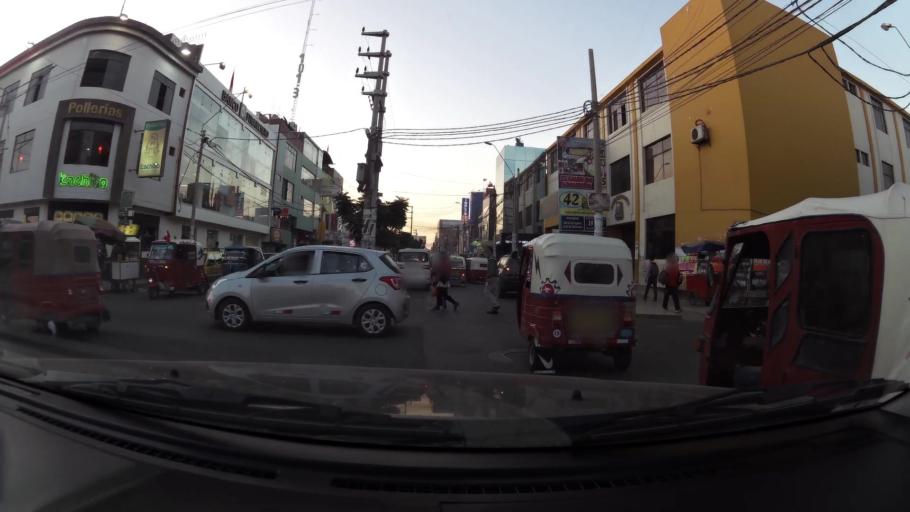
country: PE
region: Ica
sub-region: Provincia de Ica
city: Ica
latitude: -14.0661
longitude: -75.7301
